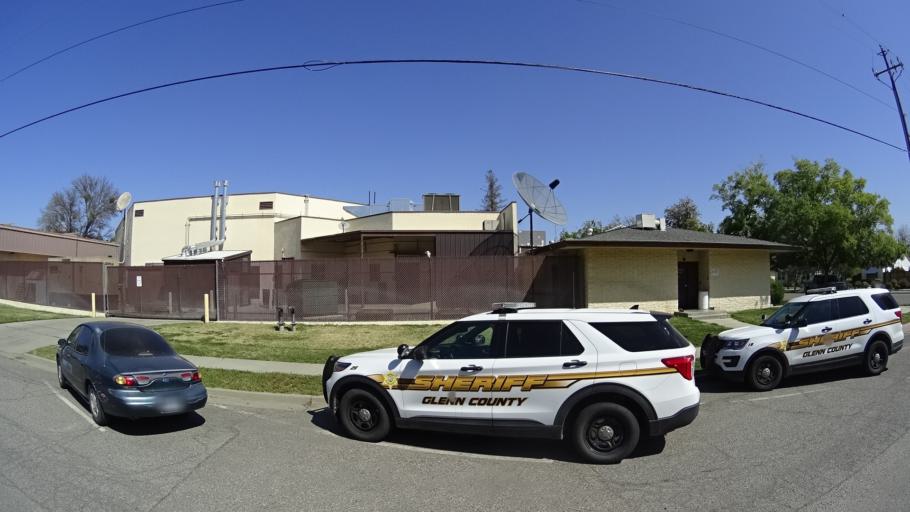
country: US
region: California
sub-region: Glenn County
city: Willows
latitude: 39.5191
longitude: -122.2000
